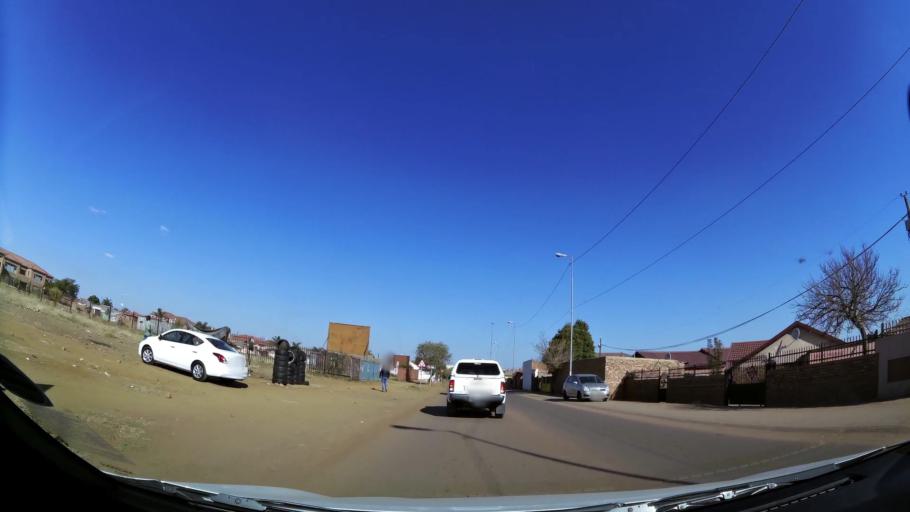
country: ZA
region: Gauteng
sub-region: City of Tshwane Metropolitan Municipality
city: Cullinan
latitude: -25.7165
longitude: 28.3758
